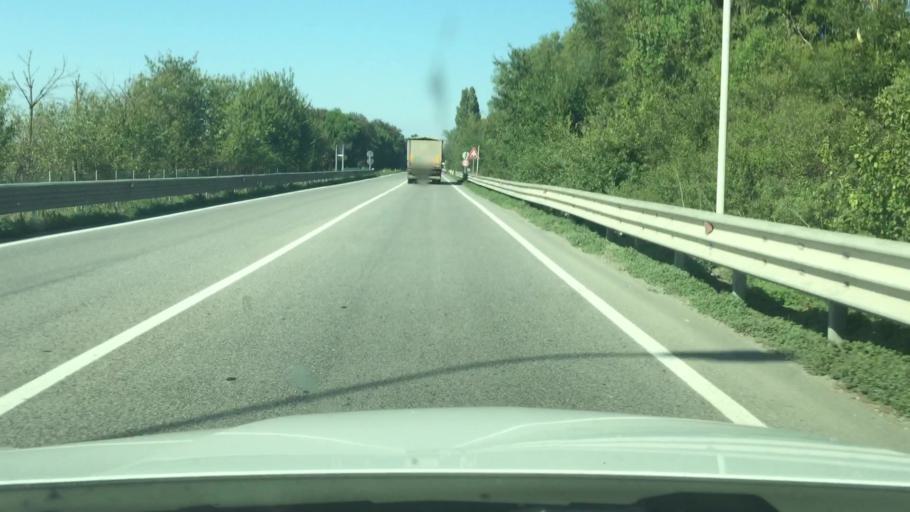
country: IT
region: Emilia-Romagna
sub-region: Provincia di Ravenna
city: Ravenna
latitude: 44.4624
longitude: 12.2089
